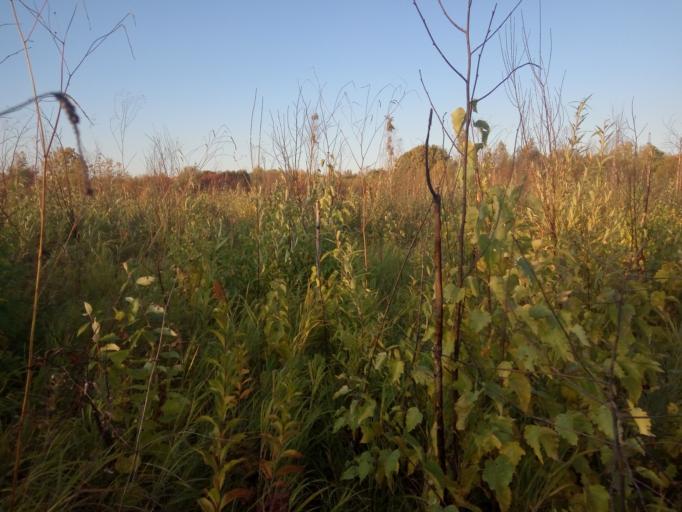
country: RU
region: Khabarovsk Krai
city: Khor
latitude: 47.7038
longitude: 134.9643
